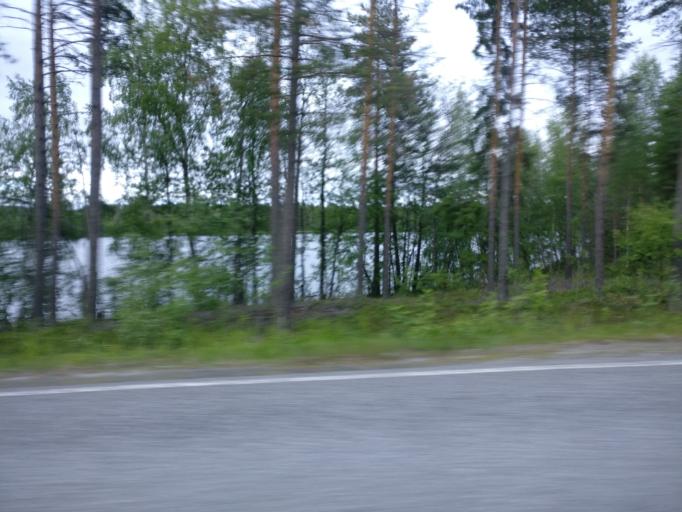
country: FI
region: Southern Savonia
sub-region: Savonlinna
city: Savonlinna
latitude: 61.9652
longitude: 28.9356
